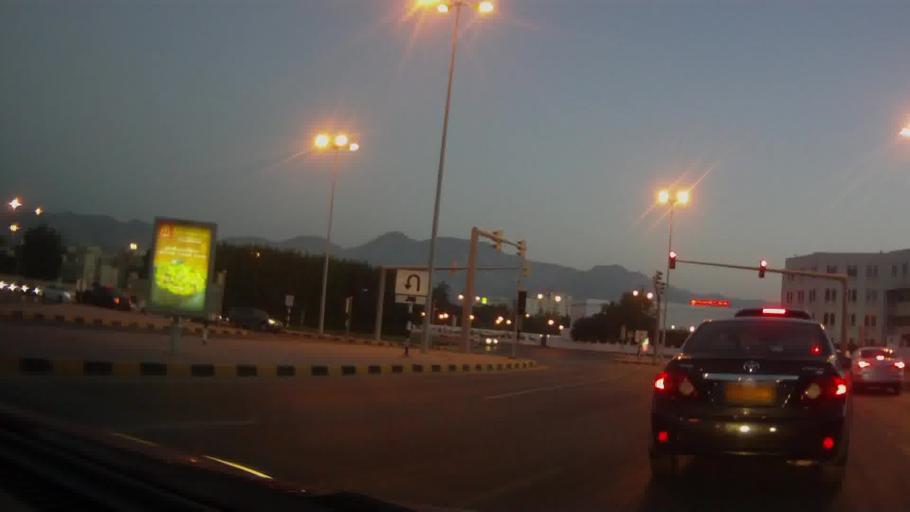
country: OM
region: Muhafazat Masqat
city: Bawshar
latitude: 23.6011
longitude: 58.4414
